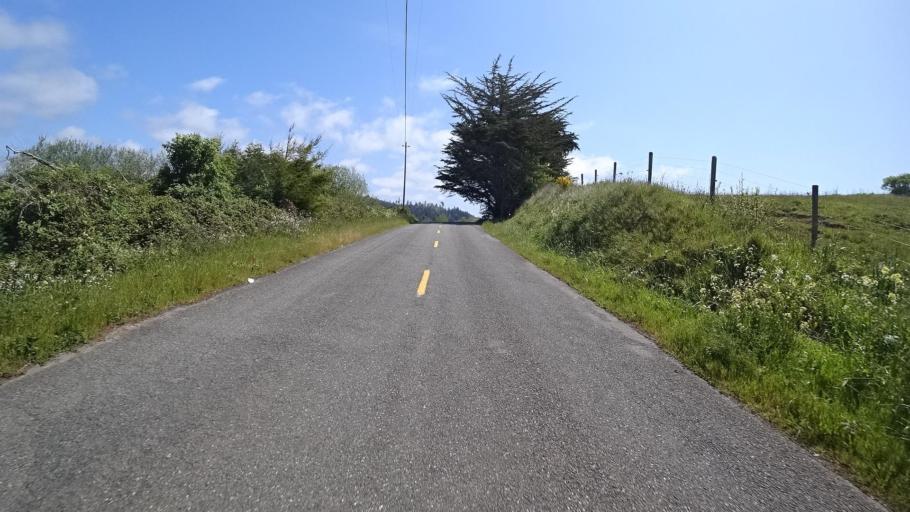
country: US
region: California
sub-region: Humboldt County
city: Humboldt Hill
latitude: 40.6689
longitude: -124.2076
